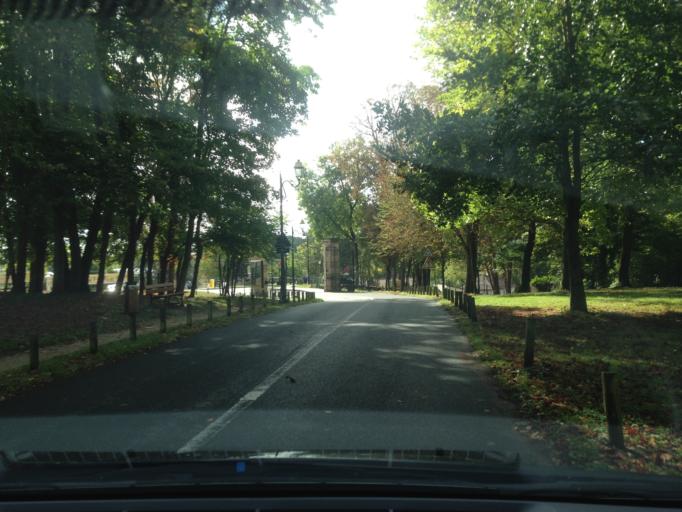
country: FR
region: Ile-de-France
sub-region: Departement du Val-d'Oise
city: Osny
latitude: 49.0642
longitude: 2.0639
